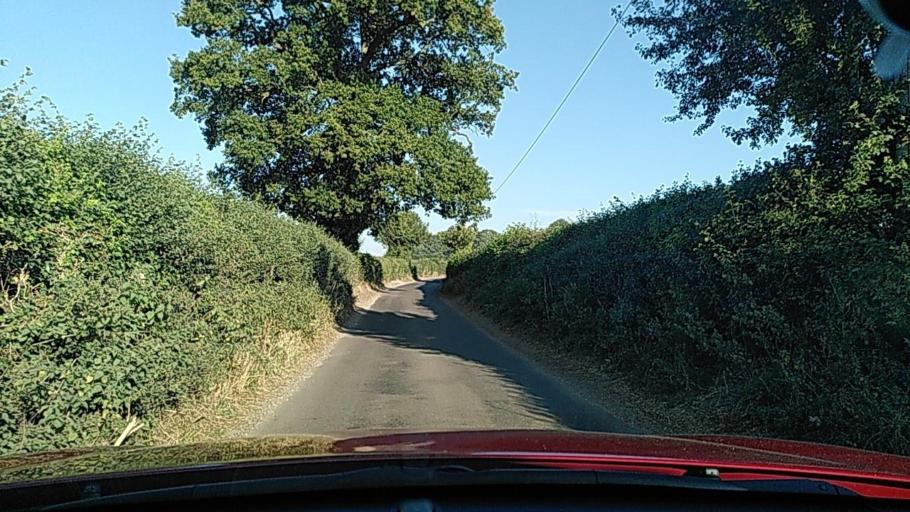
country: GB
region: England
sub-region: Wokingham
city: Sonning
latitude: 51.4904
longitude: -0.9422
